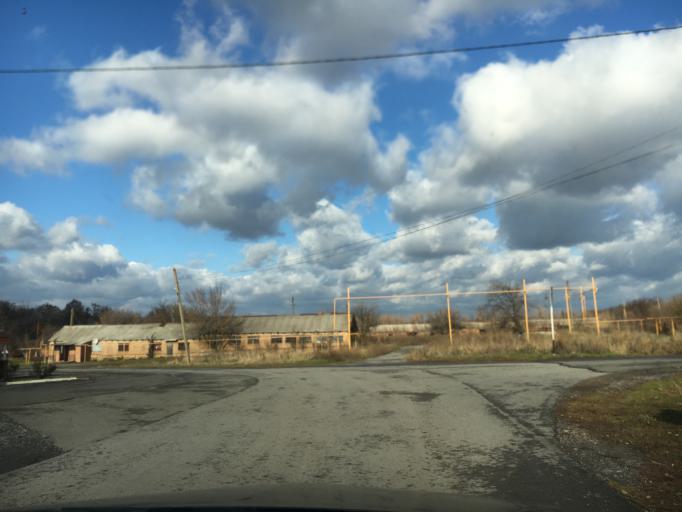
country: RU
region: Rostov
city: Pokrovskoye
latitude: 47.4817
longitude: 38.9147
